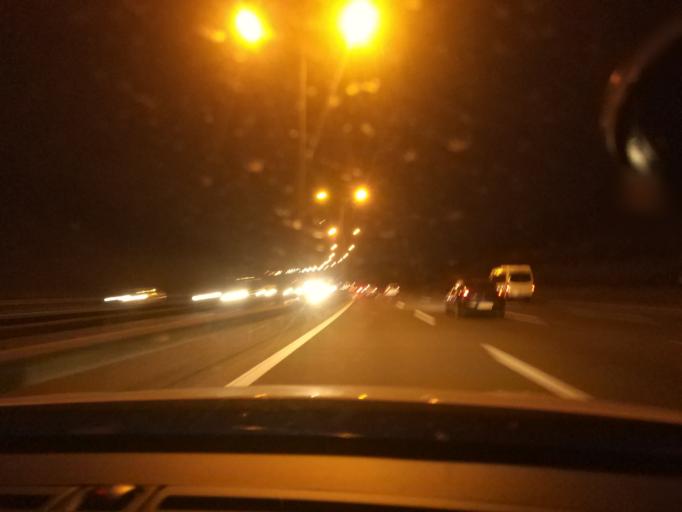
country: TR
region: Istanbul
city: Umraniye
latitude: 41.0809
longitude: 29.0959
